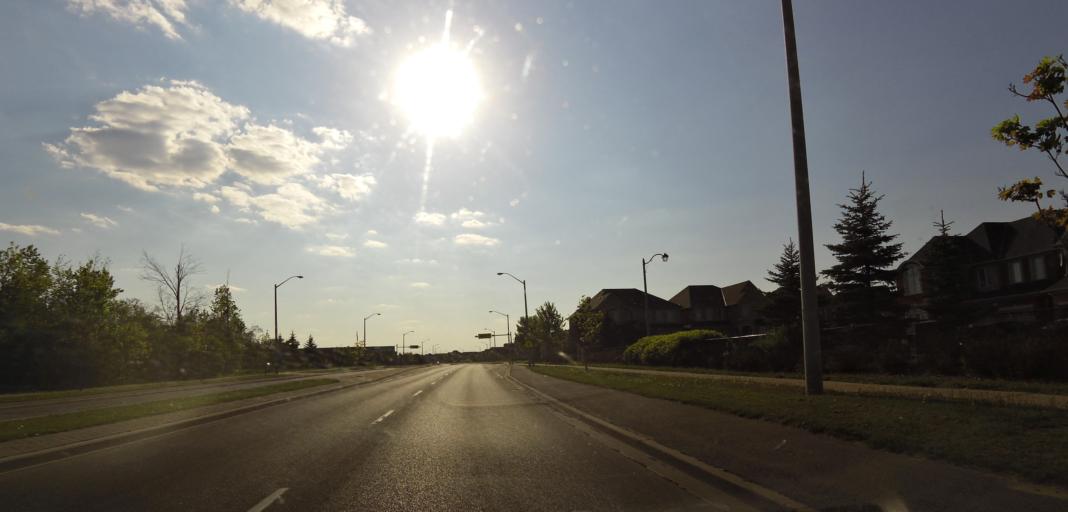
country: CA
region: Ontario
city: Brampton
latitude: 43.7664
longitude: -79.7390
